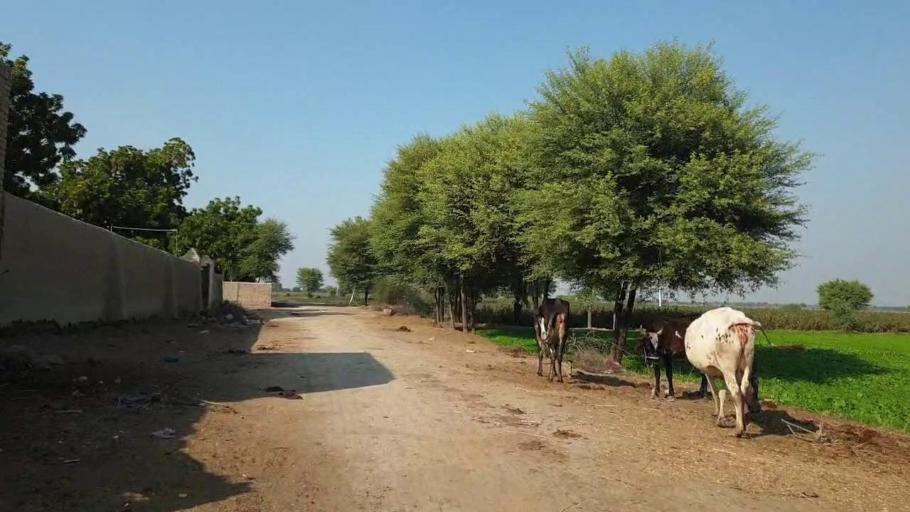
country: PK
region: Sindh
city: Sehwan
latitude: 26.4500
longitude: 67.8175
